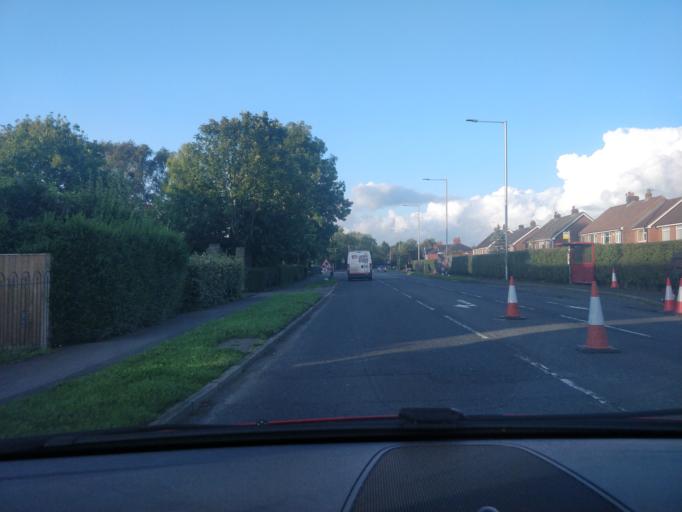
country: GB
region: England
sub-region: Lancashire
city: Preston
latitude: 53.7422
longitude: -2.7472
